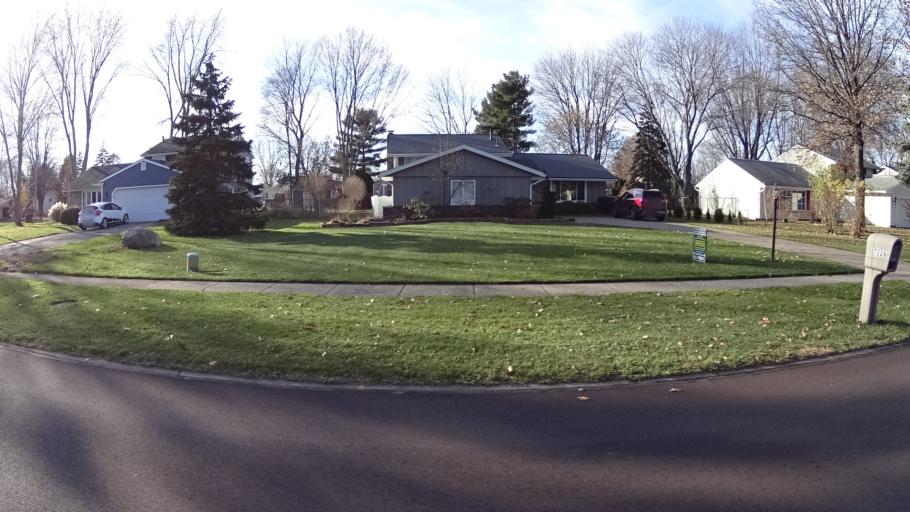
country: US
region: Ohio
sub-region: Lorain County
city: North Ridgeville
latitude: 41.3867
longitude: -81.9976
